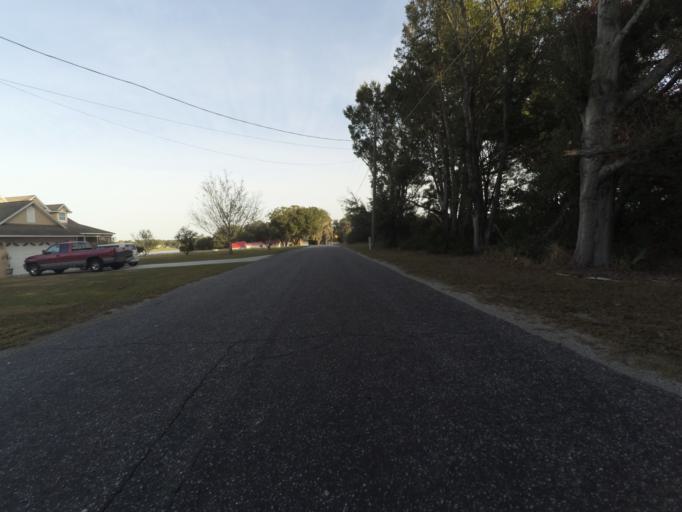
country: US
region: Florida
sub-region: Lake County
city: Umatilla
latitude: 28.9381
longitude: -81.6569
